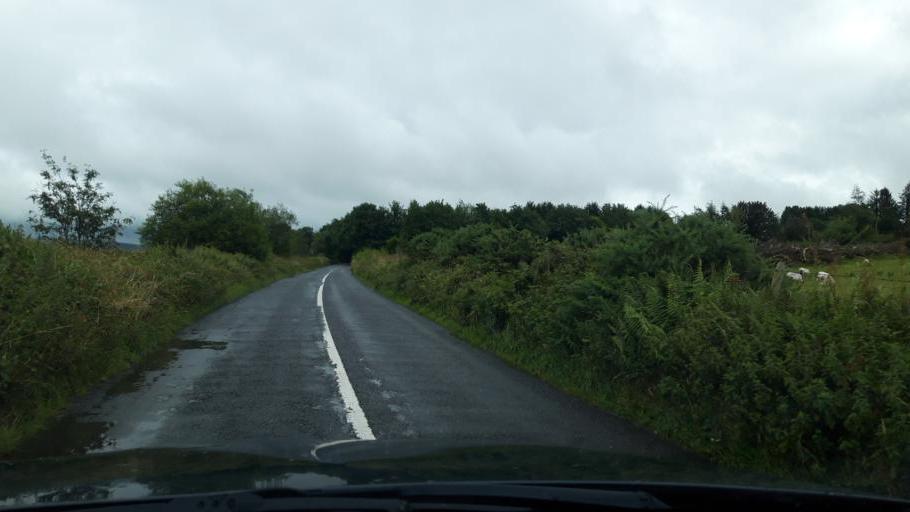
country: IE
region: Munster
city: Cahir
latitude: 52.1833
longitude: -7.8832
